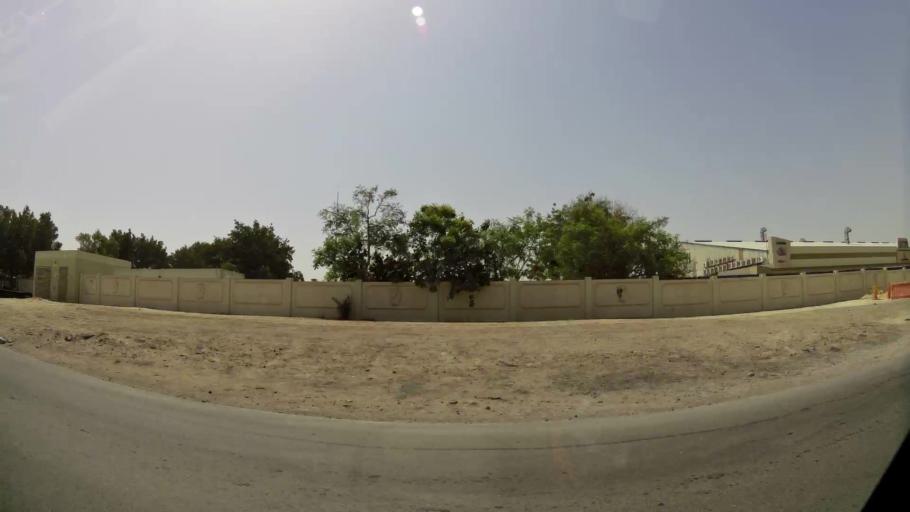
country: AE
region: Dubai
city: Dubai
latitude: 25.1459
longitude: 55.2394
